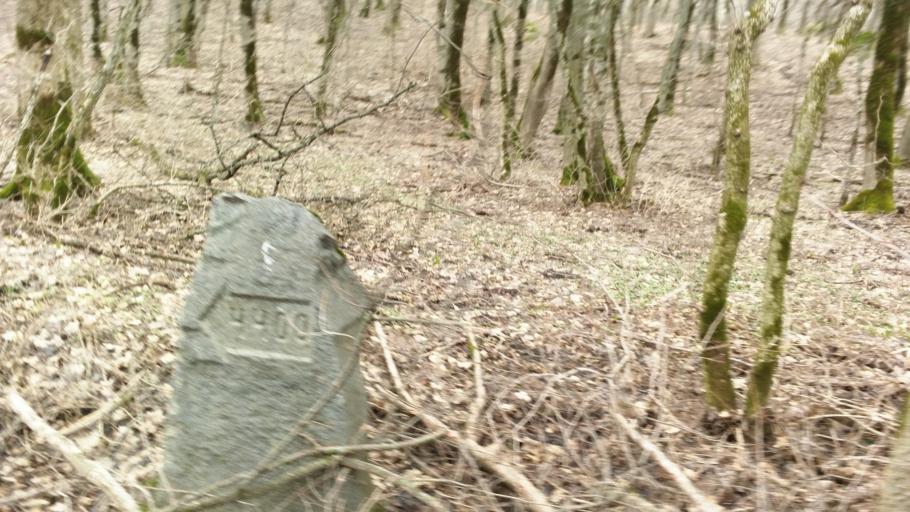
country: RU
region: Stavropol'skiy
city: Zheleznovodsk
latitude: 44.1583
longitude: 43.0407
